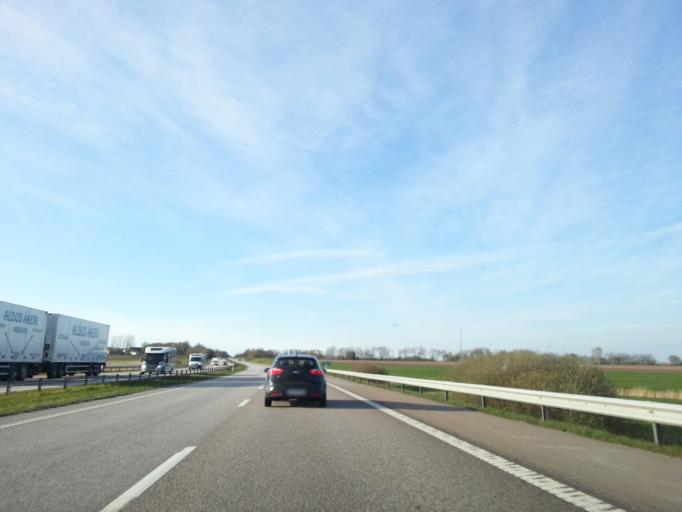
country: SE
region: Skane
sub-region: Angelholms Kommun
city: Strovelstorp
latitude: 56.1466
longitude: 12.8445
